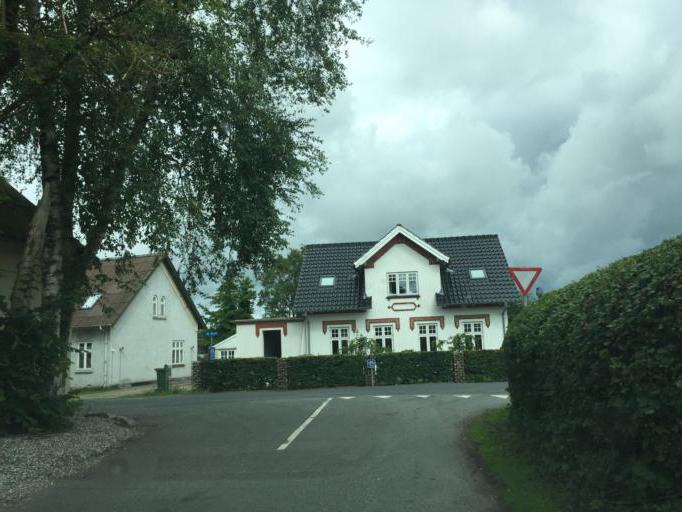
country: DK
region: South Denmark
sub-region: Faaborg-Midtfyn Kommune
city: Arslev
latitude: 55.2974
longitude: 10.4670
